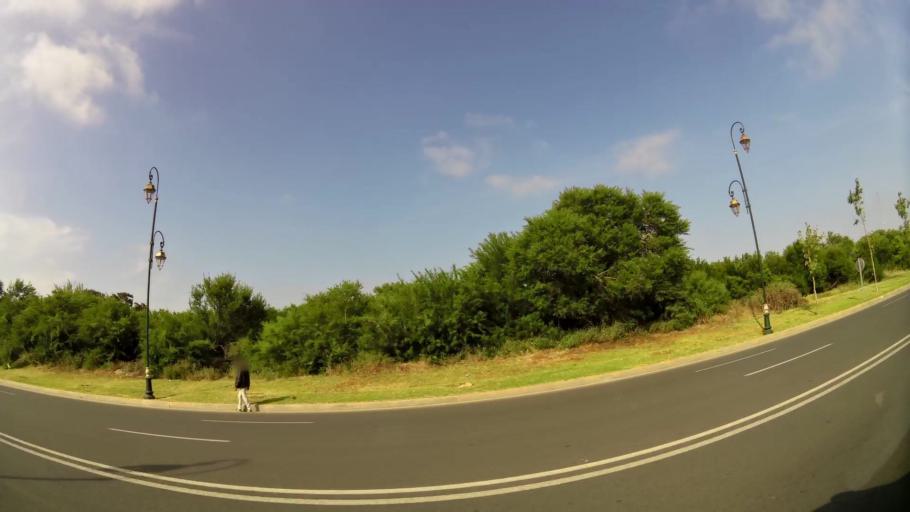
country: MA
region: Rabat-Sale-Zemmour-Zaer
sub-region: Rabat
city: Rabat
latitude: 33.9509
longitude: -6.8133
